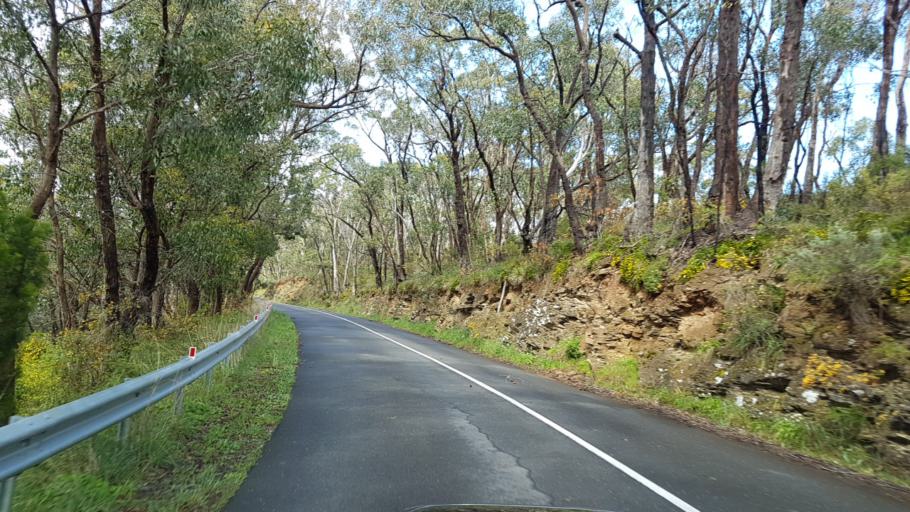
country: AU
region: South Australia
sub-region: Adelaide Hills
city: Adelaide Hills
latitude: -34.9109
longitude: 138.7577
